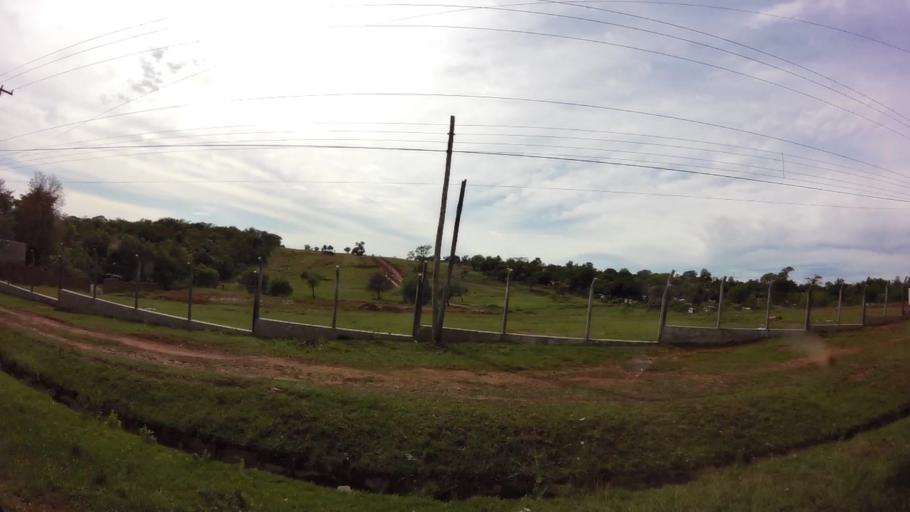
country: PY
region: Central
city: Limpio
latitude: -25.1480
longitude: -57.4598
